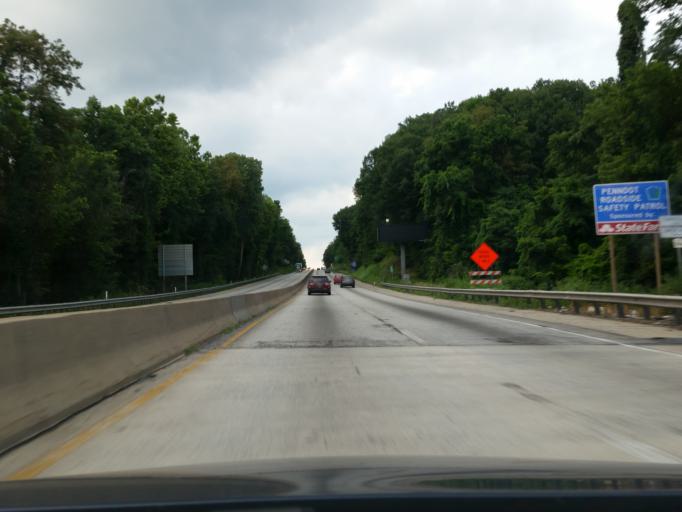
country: US
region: Pennsylvania
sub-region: Cumberland County
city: New Cumberland
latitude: 40.2172
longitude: -76.8824
